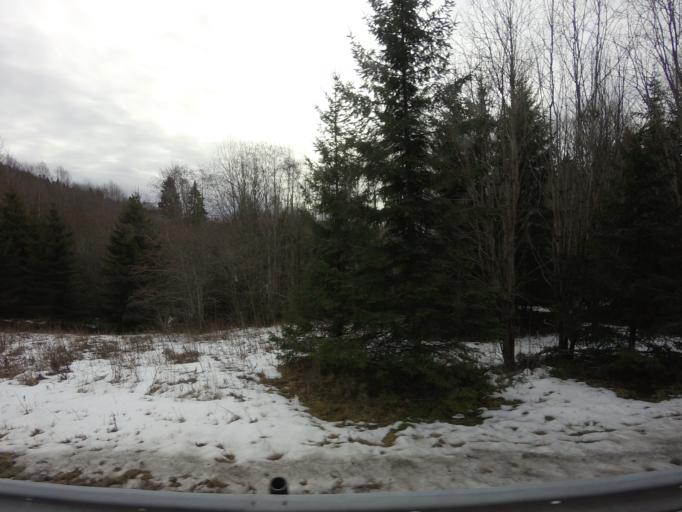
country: NO
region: Akershus
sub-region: Fet
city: Fetsund
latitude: 59.8860
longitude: 11.2114
